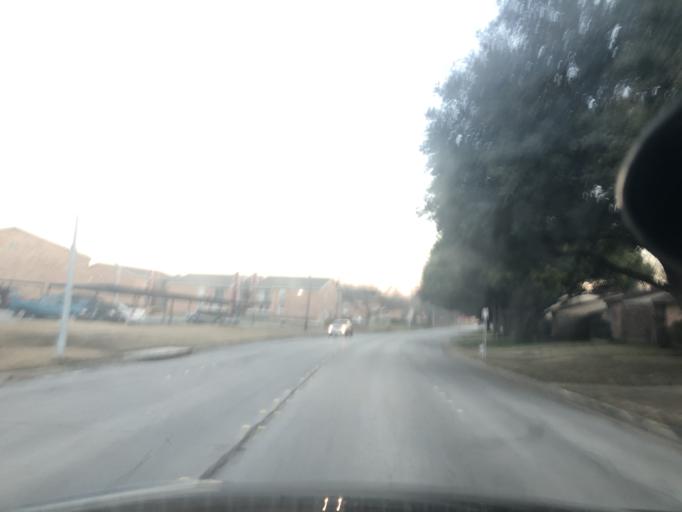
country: US
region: Texas
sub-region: Tarrant County
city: White Settlement
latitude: 32.7324
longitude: -97.4714
